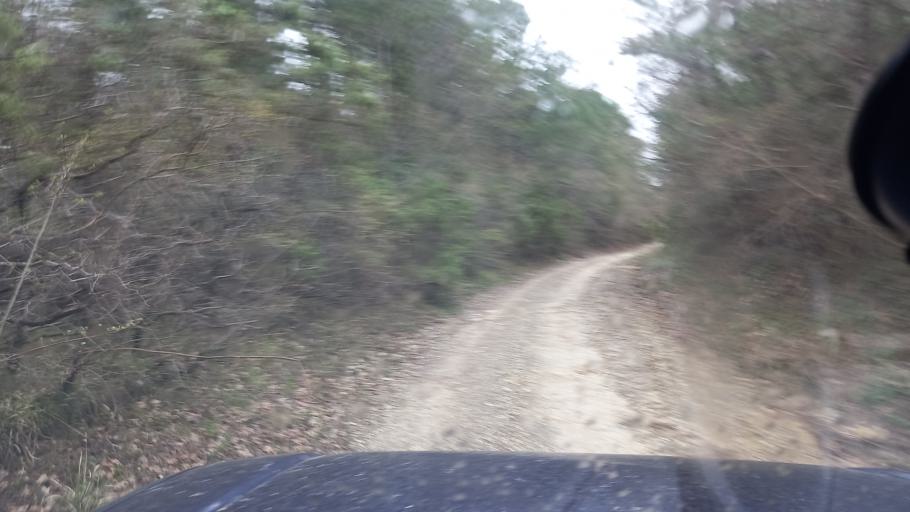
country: RU
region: Krasnodarskiy
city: Arkhipo-Osipovka
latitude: 44.3762
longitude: 38.4615
